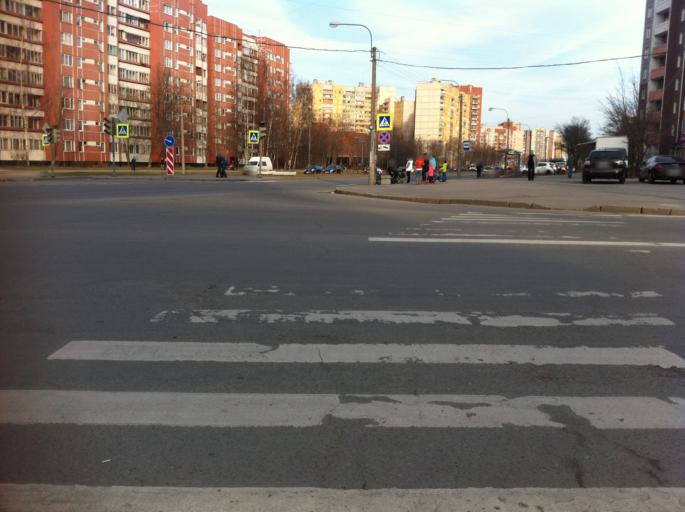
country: RU
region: St.-Petersburg
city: Uritsk
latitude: 59.8552
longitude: 30.1854
